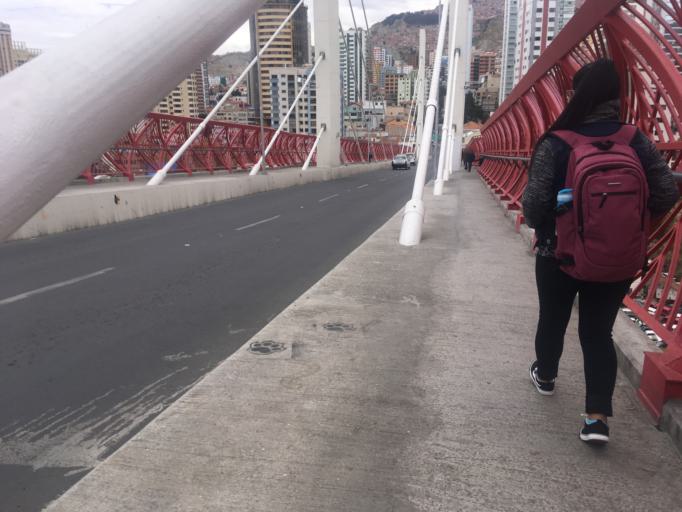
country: BO
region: La Paz
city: La Paz
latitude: -16.5060
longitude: -68.1232
